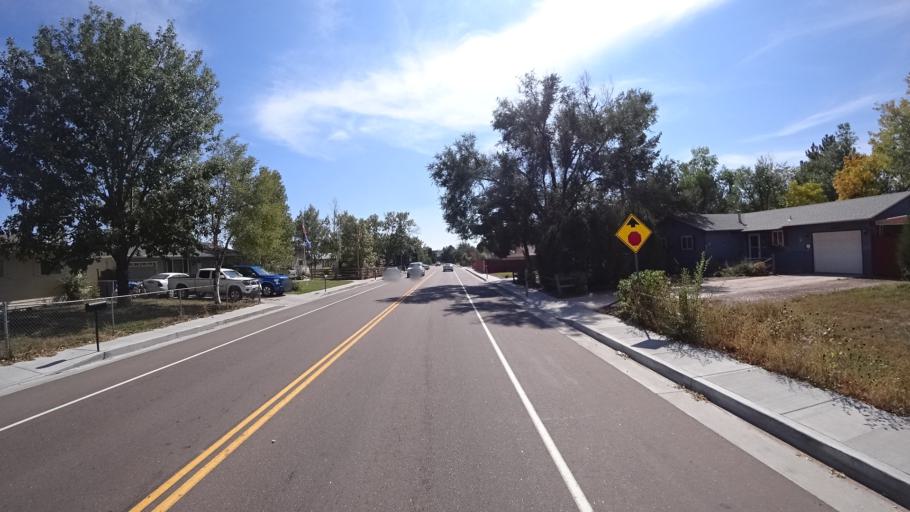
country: US
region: Colorado
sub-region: El Paso County
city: Cimarron Hills
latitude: 38.8987
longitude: -104.7528
